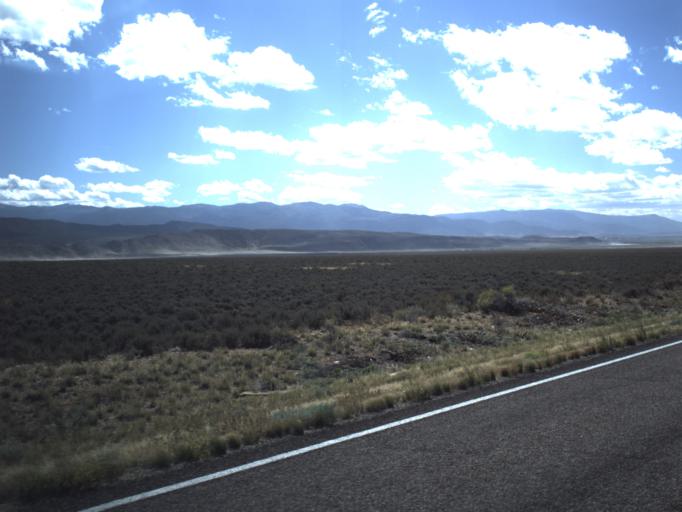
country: US
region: Utah
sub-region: Iron County
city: Enoch
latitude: 37.9461
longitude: -113.0184
